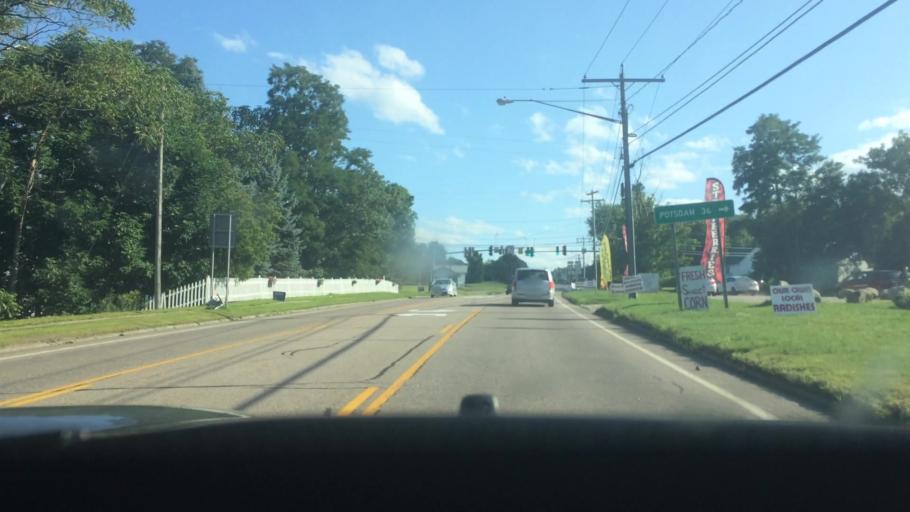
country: US
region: New York
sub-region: Franklin County
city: Malone
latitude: 44.8456
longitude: -74.3007
